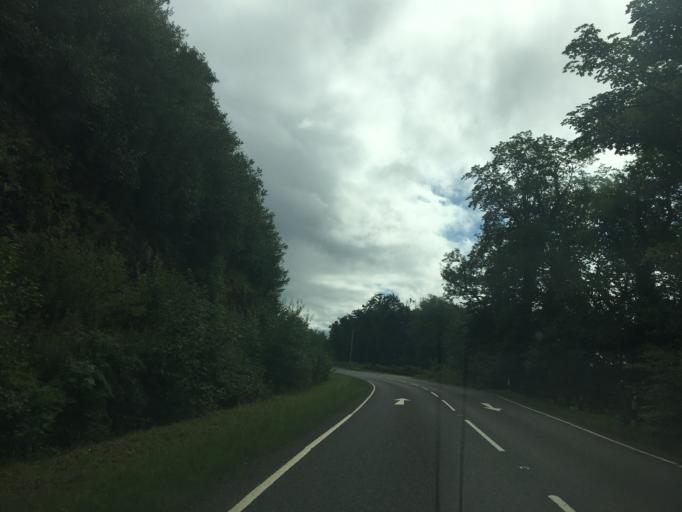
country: GB
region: Scotland
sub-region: Argyll and Bute
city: Lochgilphead
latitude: 56.1228
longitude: -5.4914
